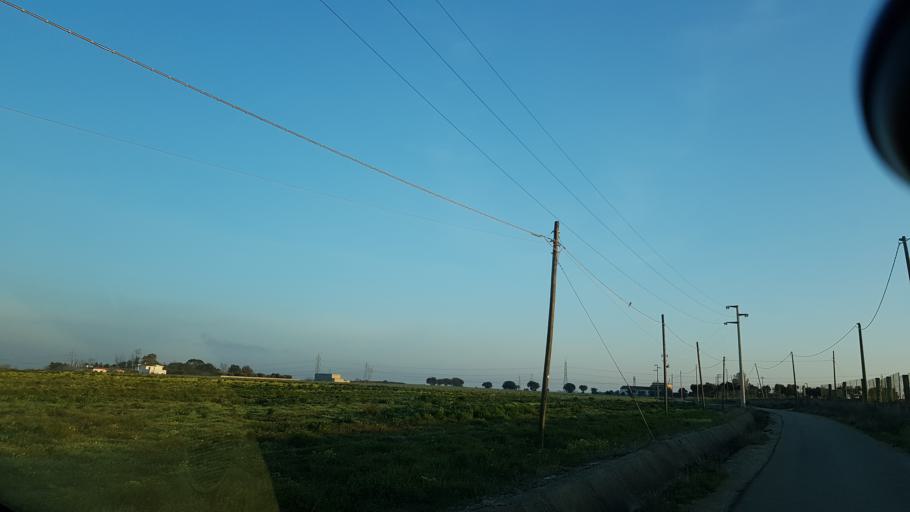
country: IT
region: Apulia
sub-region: Provincia di Brindisi
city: La Rosa
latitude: 40.6071
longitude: 17.9382
